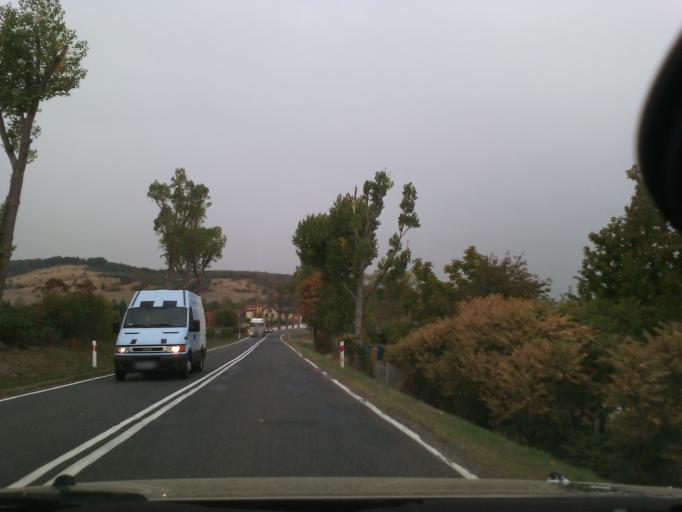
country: PL
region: Lower Silesian Voivodeship
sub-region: Powiat swidnicki
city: Swiebodzice
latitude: 50.8654
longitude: 16.3027
